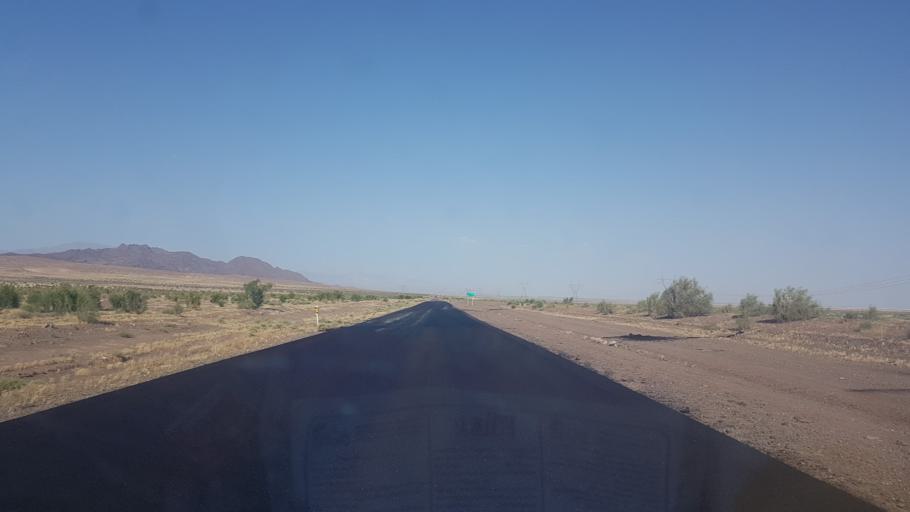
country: IR
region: Razavi Khorasan
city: Joghatay
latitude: 36.3629
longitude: 56.6022
